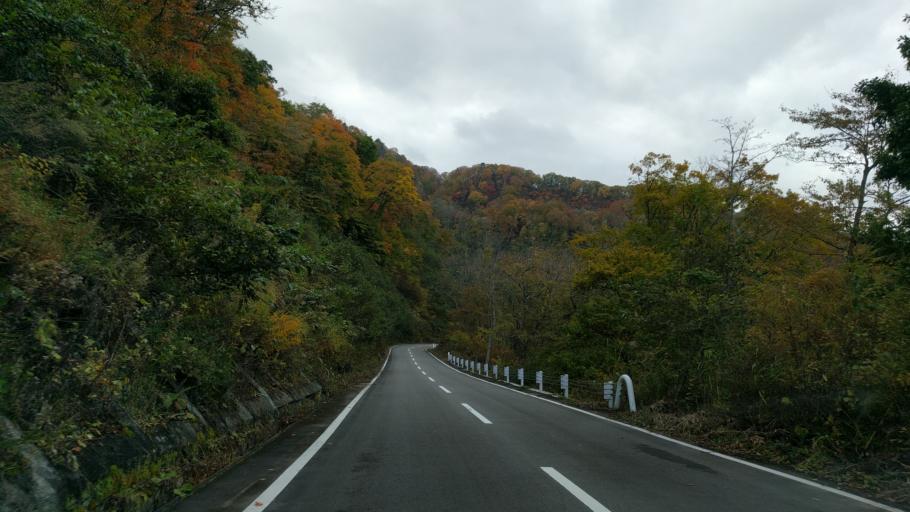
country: JP
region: Fukushima
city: Kitakata
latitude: 37.3833
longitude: 139.6977
